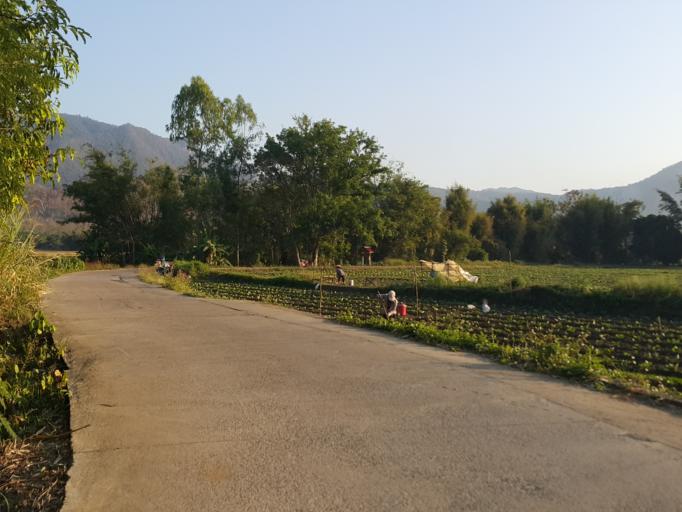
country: TH
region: Chiang Mai
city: Mae On
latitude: 18.7585
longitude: 99.2569
